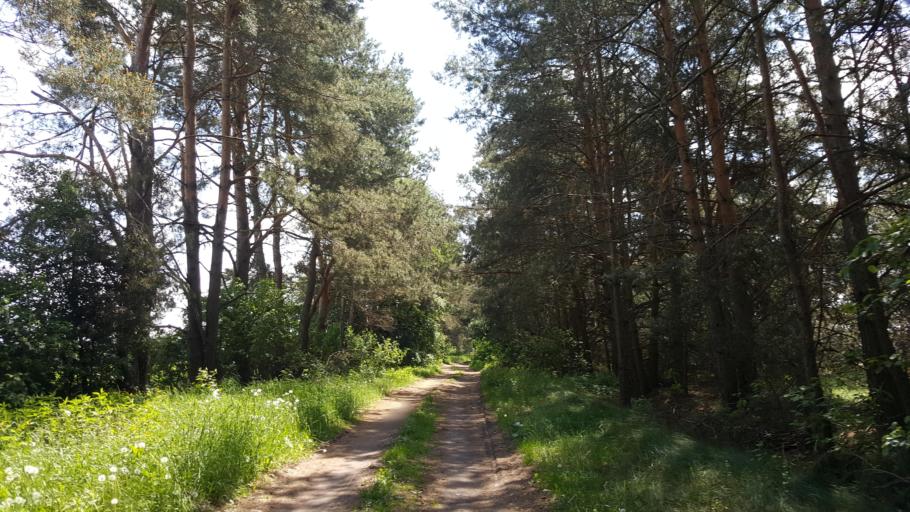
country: BY
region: Brest
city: Kamyanyets
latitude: 52.3972
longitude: 23.8572
